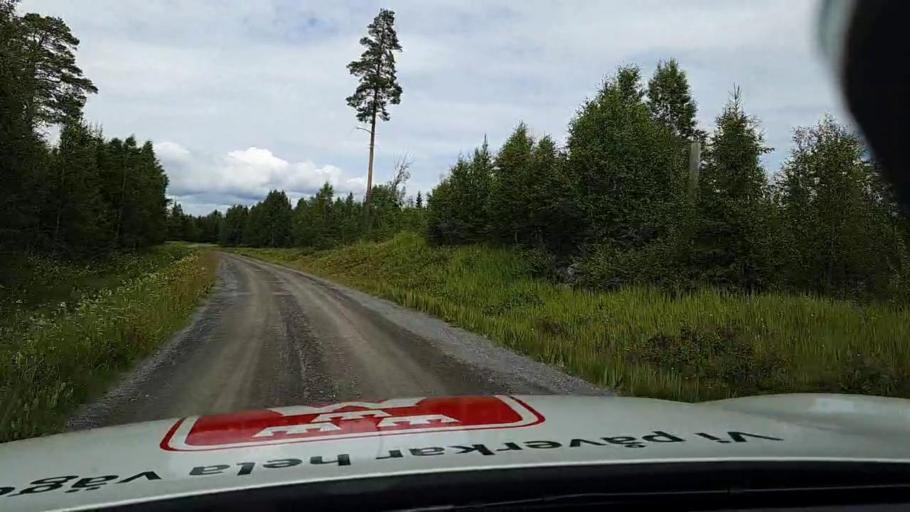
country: SE
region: Jaemtland
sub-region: OEstersunds Kommun
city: Lit
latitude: 63.3024
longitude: 15.2464
